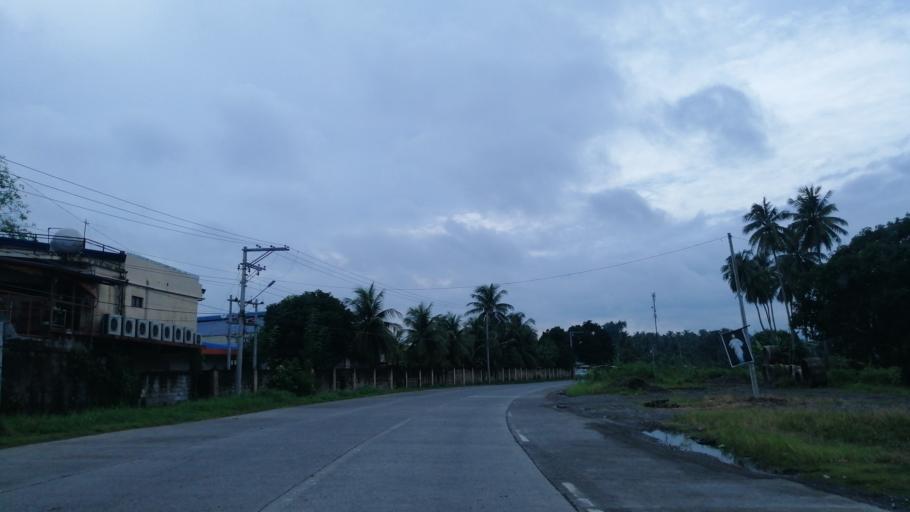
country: PH
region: Davao
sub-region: Province of Davao del Norte
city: Corocotan
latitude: 7.3991
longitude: 125.7721
